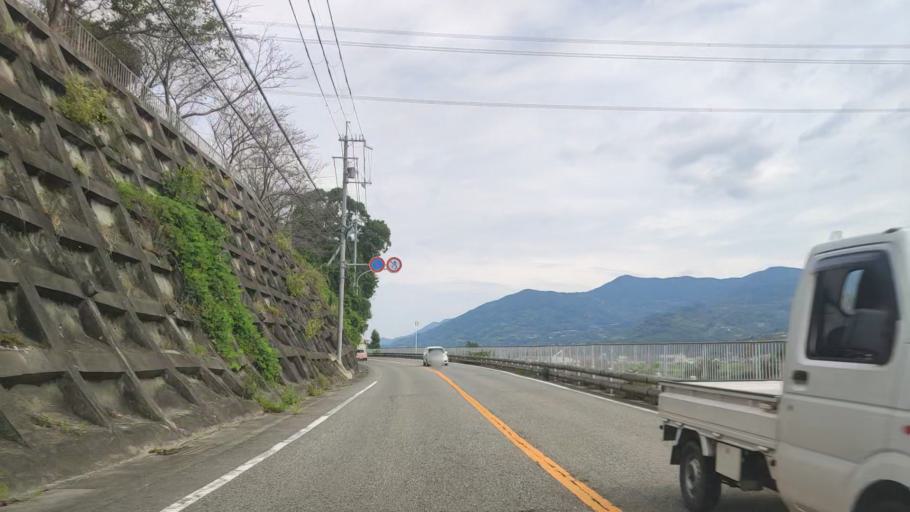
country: JP
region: Wakayama
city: Iwade
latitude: 34.2801
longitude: 135.4537
